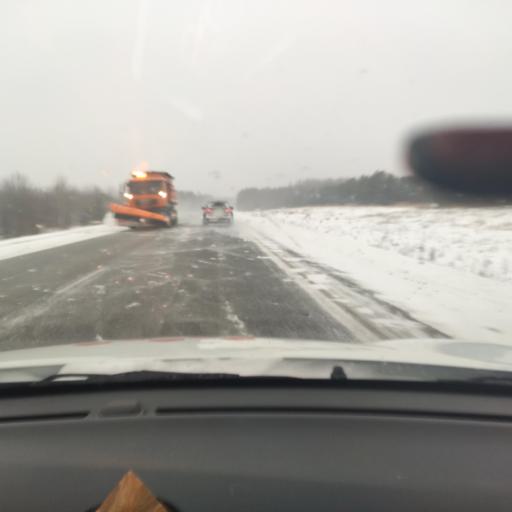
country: RU
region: Tatarstan
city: Verkhniy Uslon
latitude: 55.7010
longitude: 48.8869
